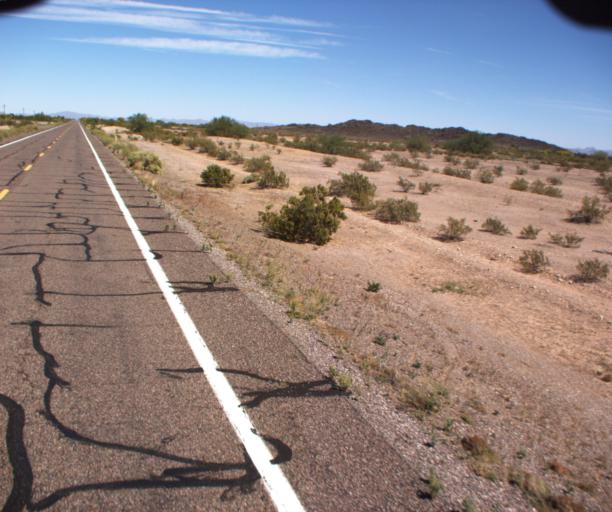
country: US
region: Arizona
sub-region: Maricopa County
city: Gila Bend
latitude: 32.7982
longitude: -112.8006
